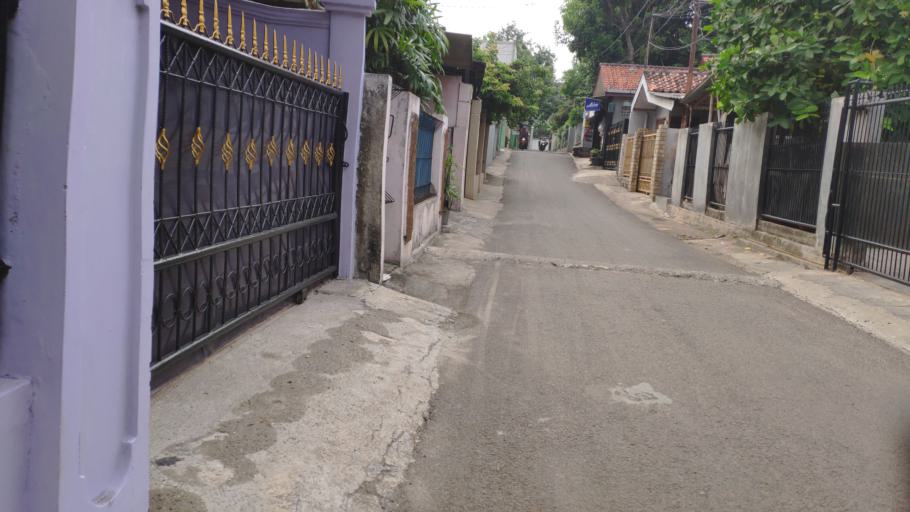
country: ID
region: West Java
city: Depok
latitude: -6.3483
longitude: 106.8114
